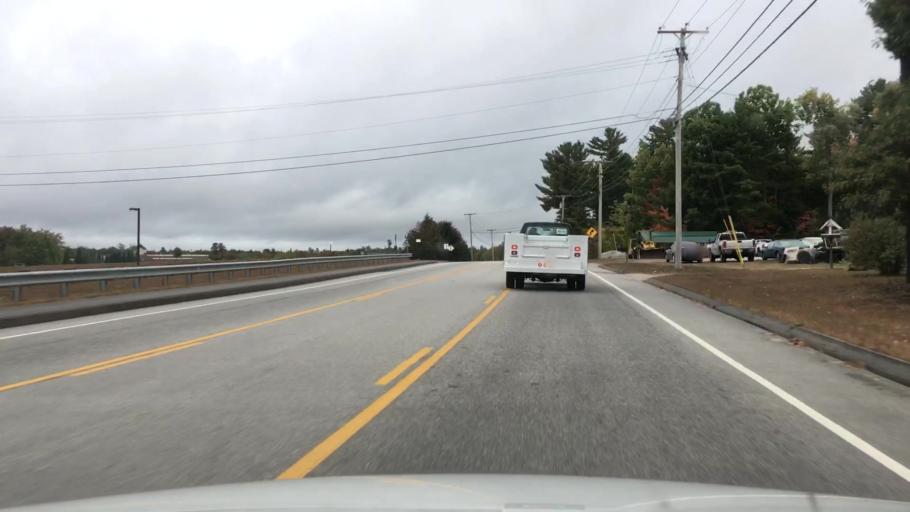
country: US
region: Maine
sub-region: Androscoggin County
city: Poland
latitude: 44.0700
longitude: -70.4079
